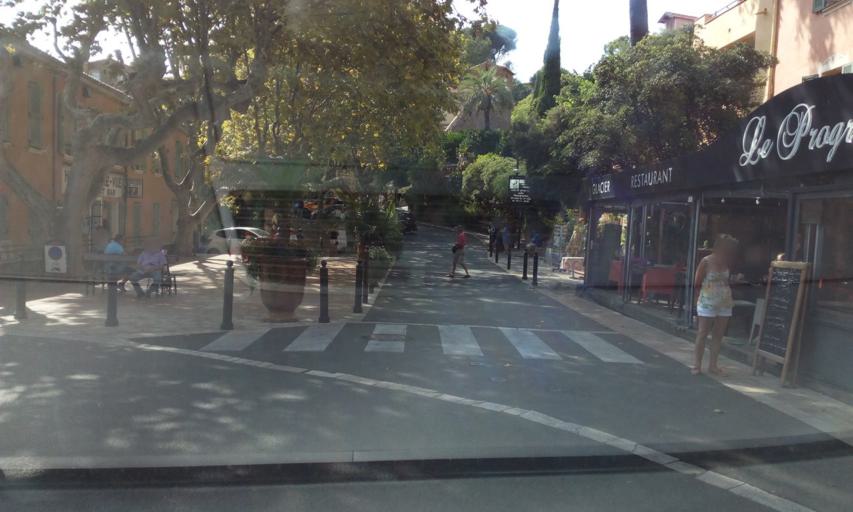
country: FR
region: Provence-Alpes-Cote d'Azur
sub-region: Departement du Var
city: Bormes-les-Mimosas
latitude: 43.1519
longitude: 6.3436
